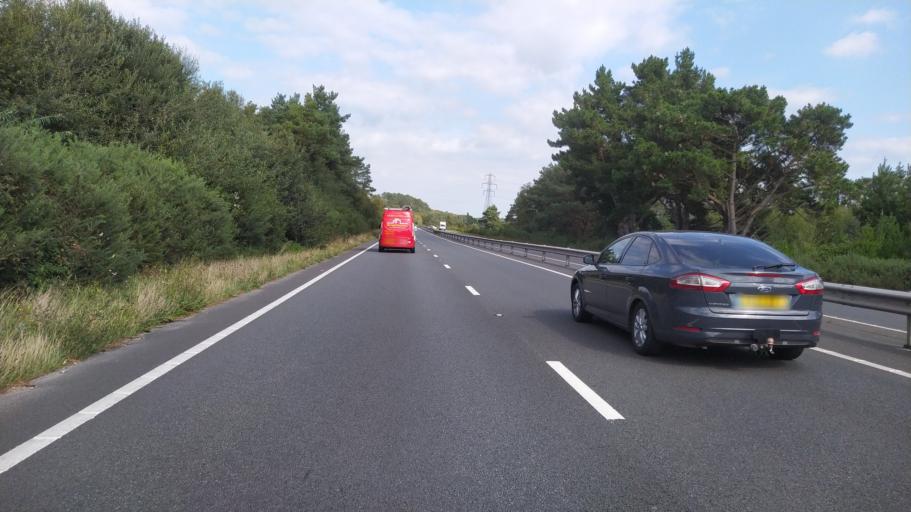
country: GB
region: England
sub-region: Dorset
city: St Leonards
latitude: 50.7955
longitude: -1.8153
